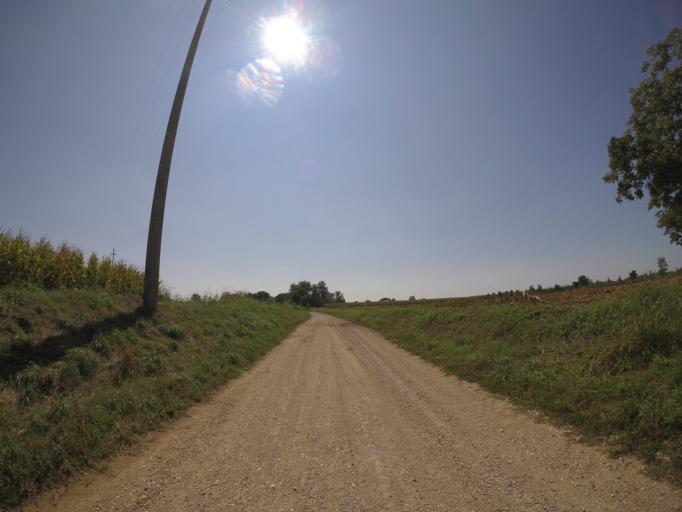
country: IT
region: Friuli Venezia Giulia
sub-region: Provincia di Udine
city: Bertiolo
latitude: 45.9438
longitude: 13.0694
